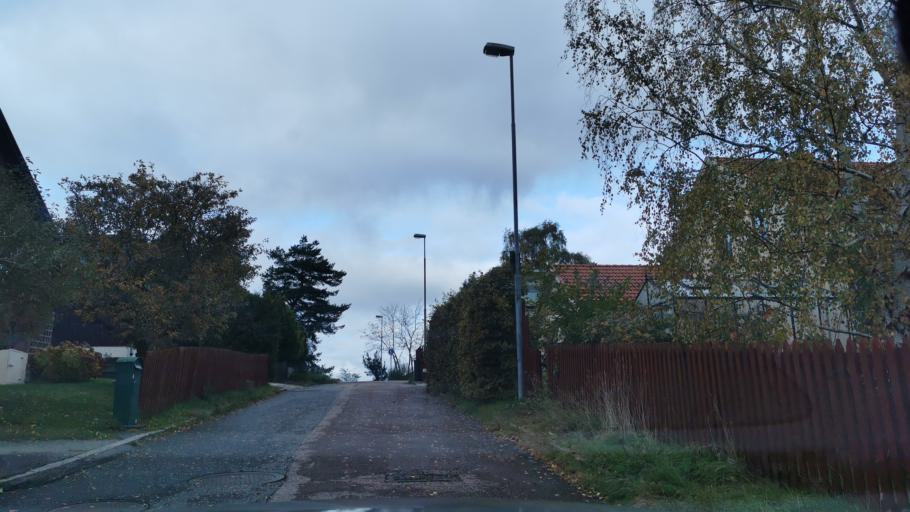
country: SE
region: Vaestra Goetaland
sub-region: Partille Kommun
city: Partille
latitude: 57.7257
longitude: 12.0713
